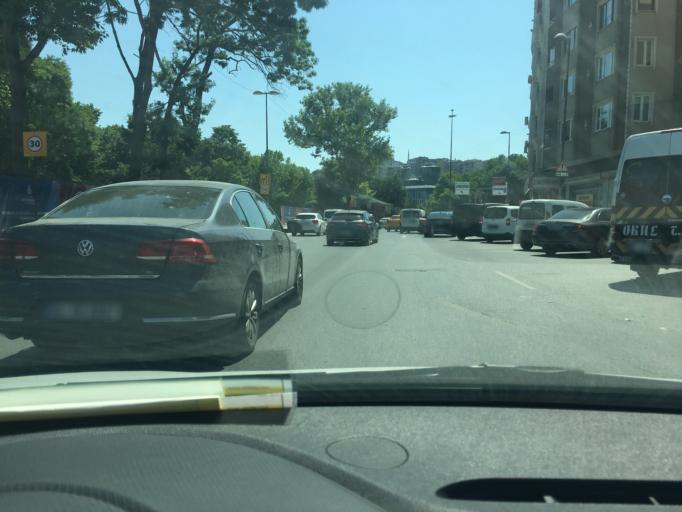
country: TR
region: Istanbul
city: Sisli
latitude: 41.0742
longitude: 28.9461
